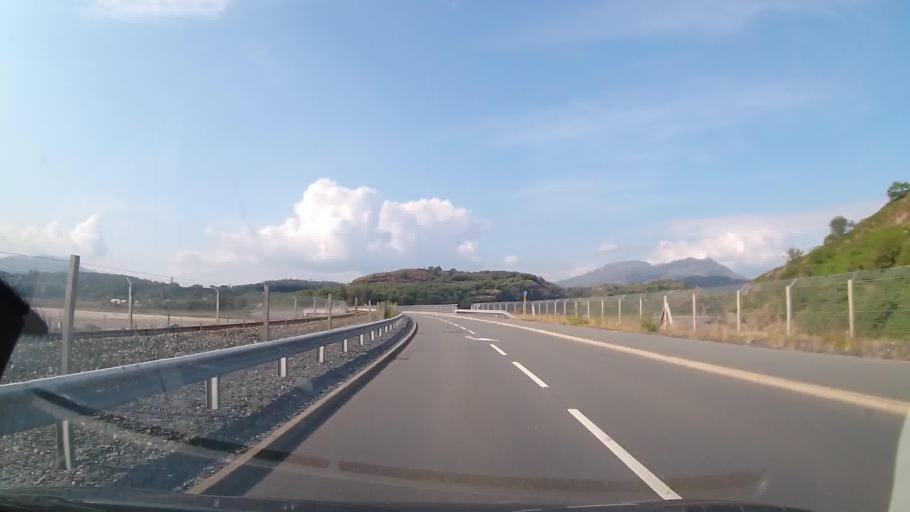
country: GB
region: Wales
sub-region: Gwynedd
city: Penrhyndeudraeth
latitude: 52.9228
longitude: -4.0557
